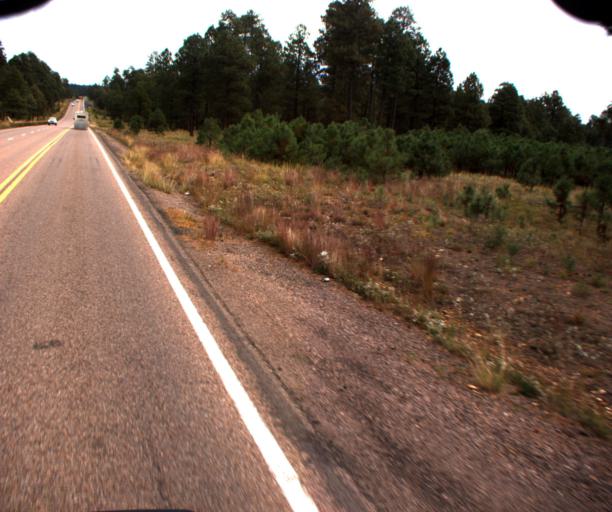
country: US
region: Arizona
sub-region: Navajo County
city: Heber-Overgaard
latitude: 34.3279
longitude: -110.8162
